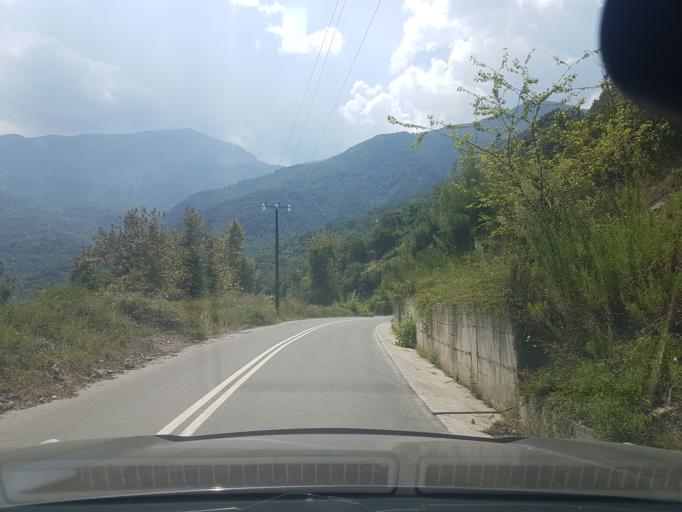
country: GR
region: Central Greece
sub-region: Nomos Evvoias
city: Kymi
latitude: 38.6327
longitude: 23.9451
